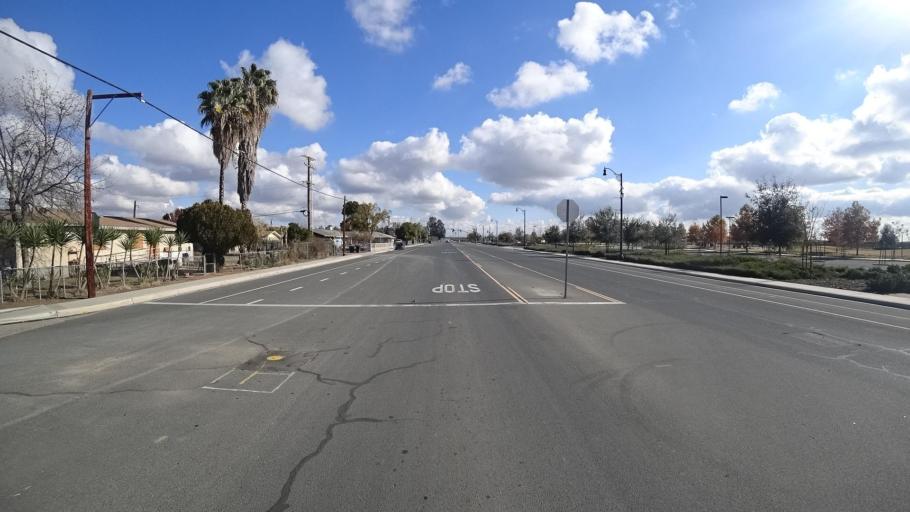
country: US
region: California
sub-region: Kern County
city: McFarland
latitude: 35.6745
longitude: -119.2207
